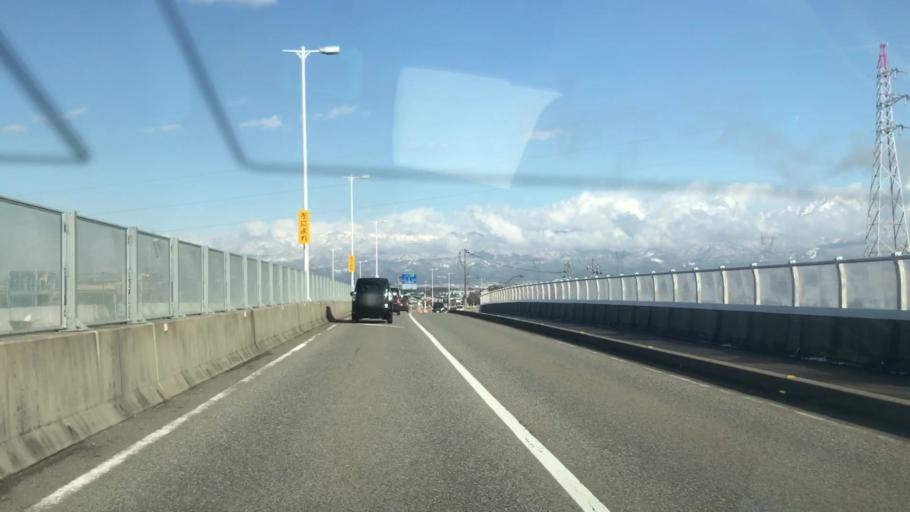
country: JP
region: Toyama
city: Toyama-shi
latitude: 36.6871
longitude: 137.2832
